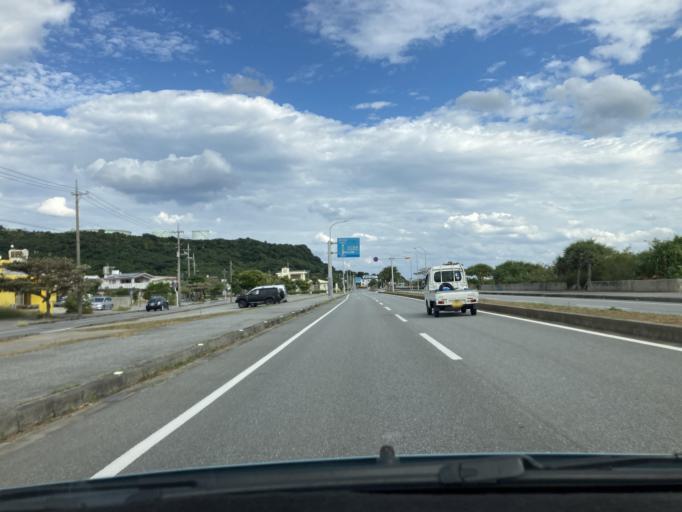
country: JP
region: Okinawa
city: Katsuren-haebaru
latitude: 26.3403
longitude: 127.9505
